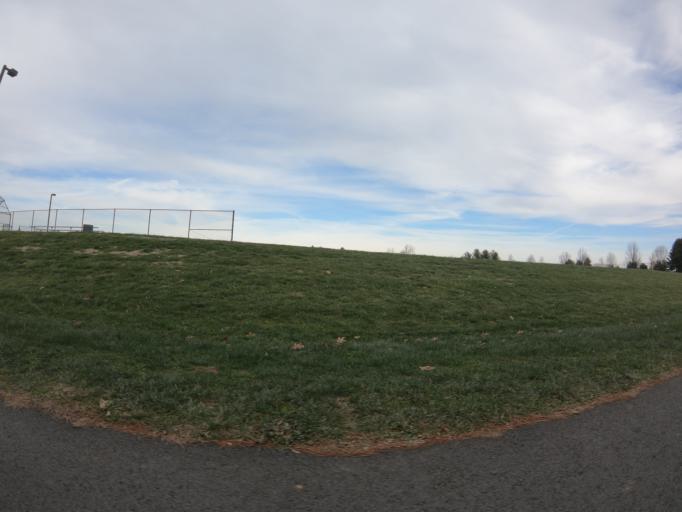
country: US
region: Maryland
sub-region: Frederick County
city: Ballenger Creek
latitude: 39.3803
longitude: -77.4460
